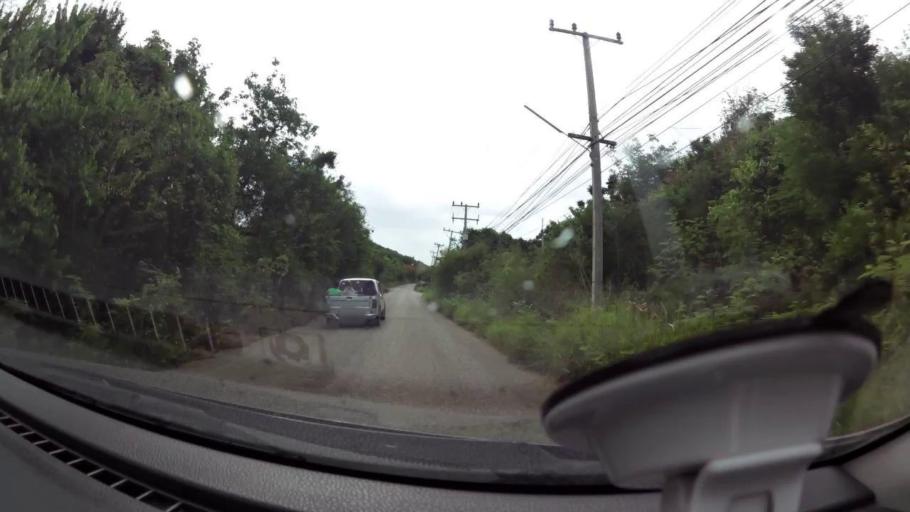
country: TH
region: Prachuap Khiri Khan
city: Pran Buri
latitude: 12.4371
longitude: 99.9731
